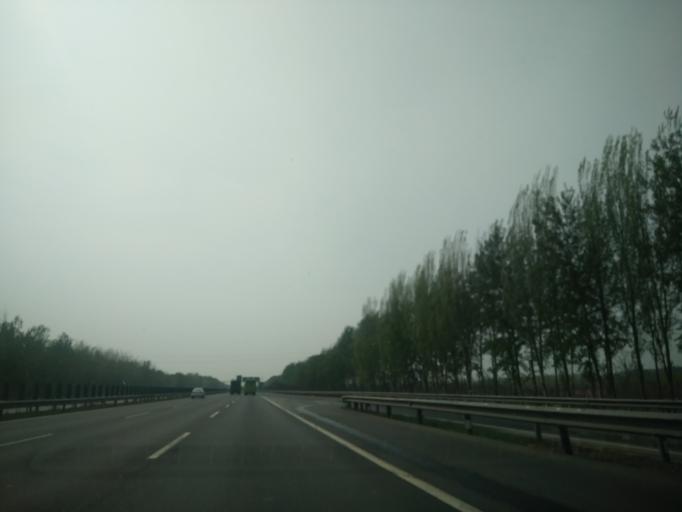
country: CN
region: Beijing
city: Xiji
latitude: 39.7991
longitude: 116.9230
